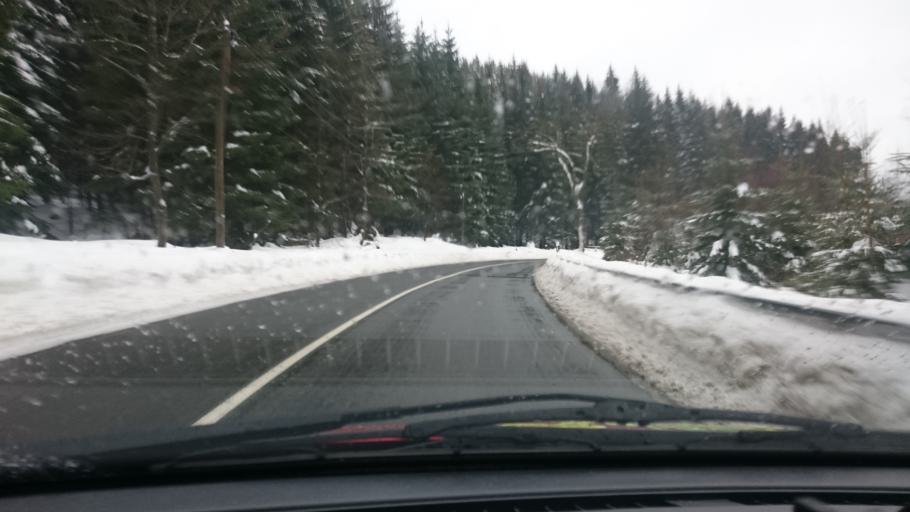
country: DE
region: Saxony
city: Tannenbergsthal
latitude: 50.4194
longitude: 12.4742
